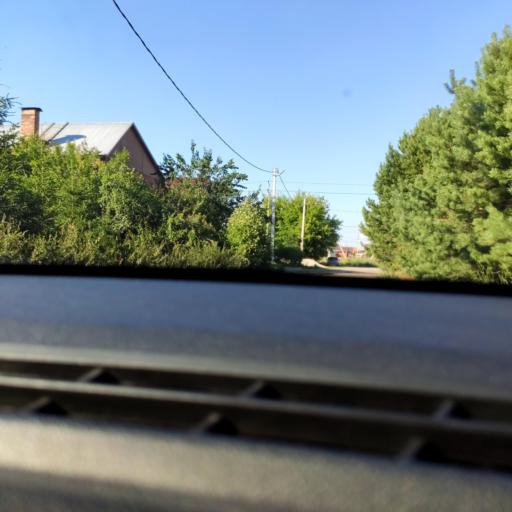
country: RU
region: Samara
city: Podstepki
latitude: 53.5704
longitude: 49.0703
